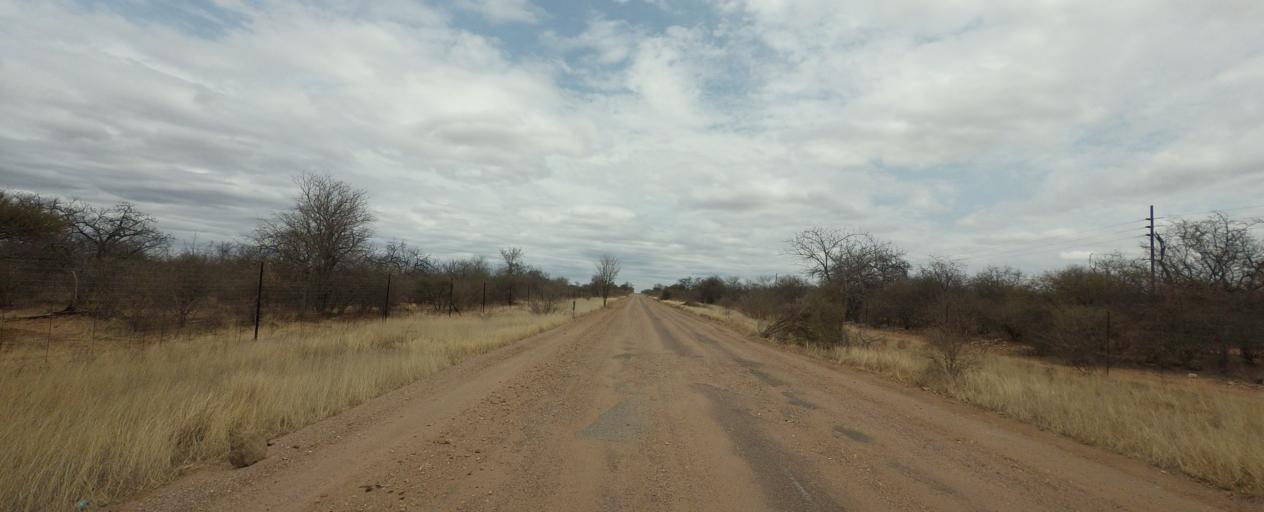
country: BW
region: Central
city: Mathathane
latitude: -22.6691
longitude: 28.6873
